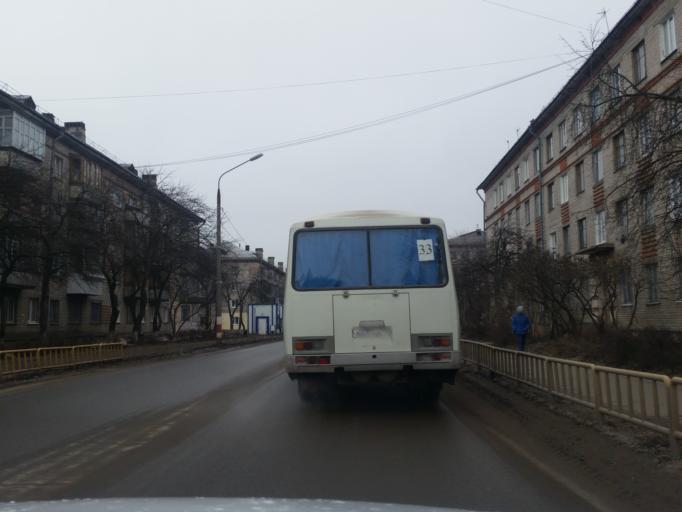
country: RU
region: Ulyanovsk
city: Dimitrovgrad
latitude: 54.2278
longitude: 49.5488
